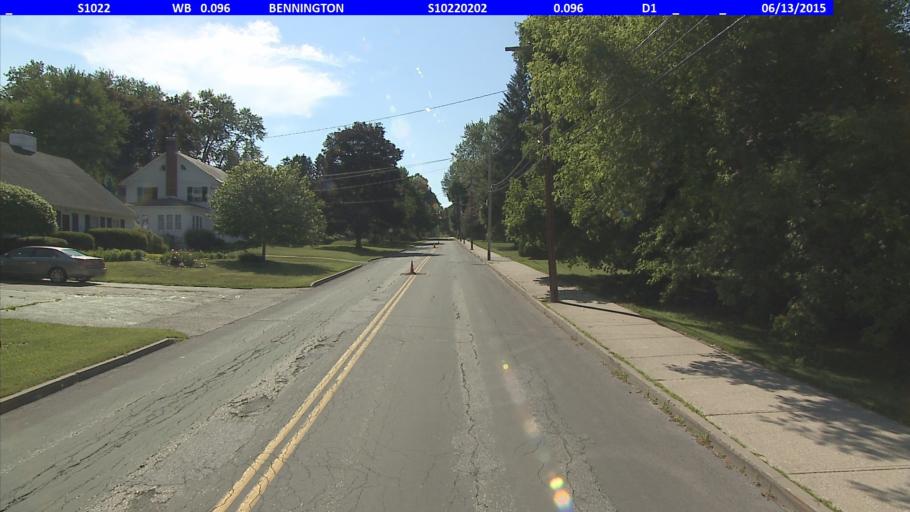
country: US
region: Vermont
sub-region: Bennington County
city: Bennington
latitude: 42.8784
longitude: -73.2079
